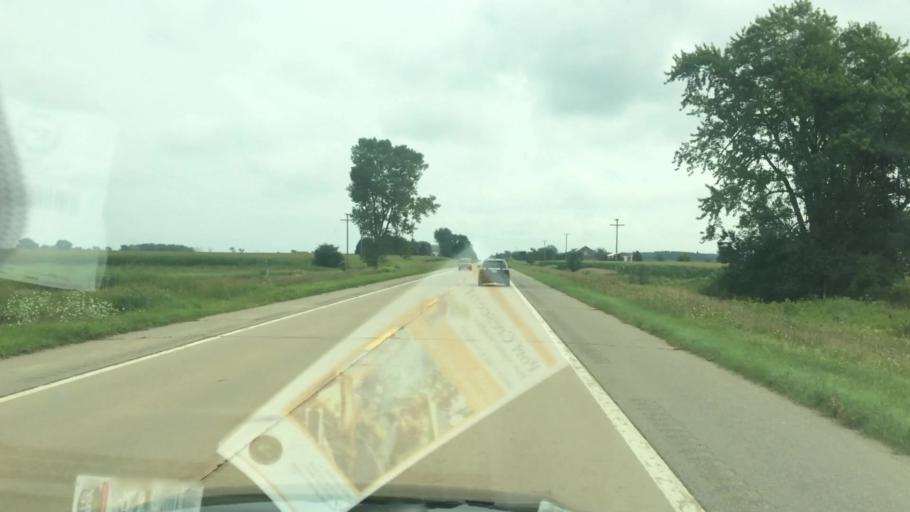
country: US
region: Michigan
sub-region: Huron County
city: Bad Axe
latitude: 44.0423
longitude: -82.9440
